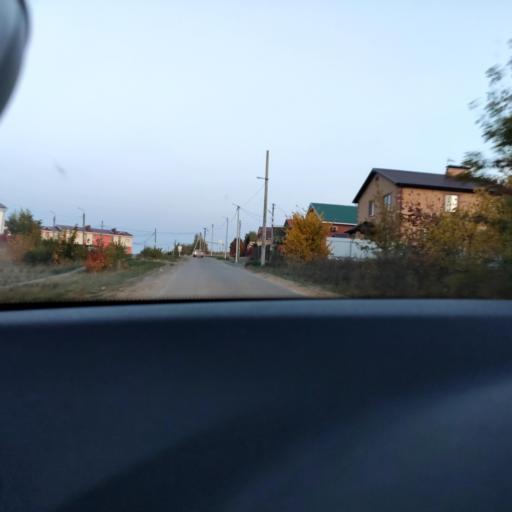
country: RU
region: Samara
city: Novosemeykino
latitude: 53.3821
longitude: 50.3226
